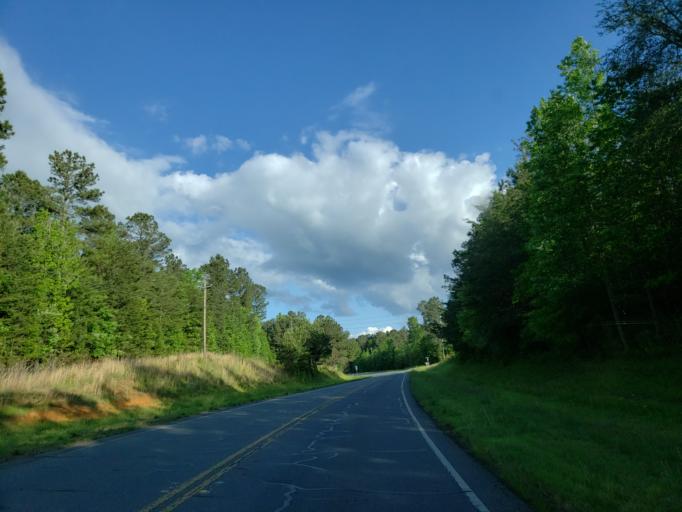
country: US
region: Georgia
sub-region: Bartow County
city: Rydal
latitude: 34.3413
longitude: -84.7436
